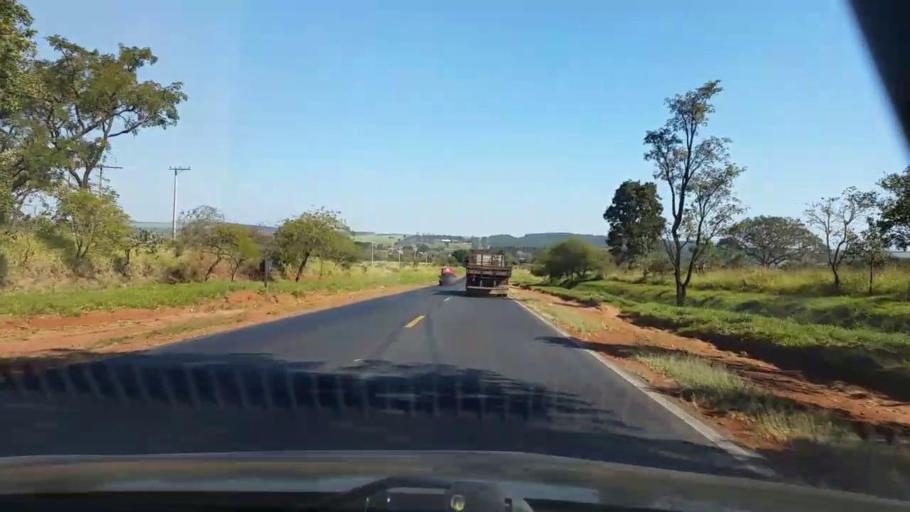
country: BR
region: Sao Paulo
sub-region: Sao Manuel
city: Sao Manuel
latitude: -22.7965
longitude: -48.6604
